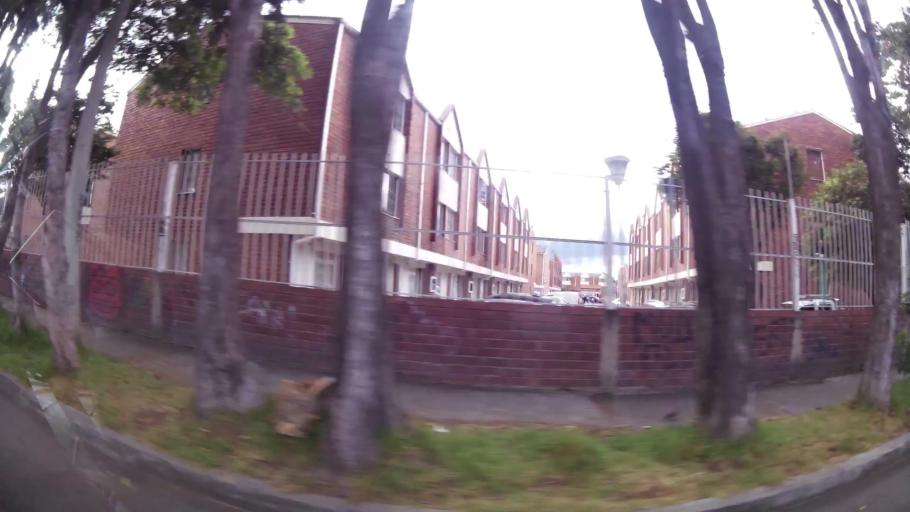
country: CO
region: Bogota D.C.
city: Bogota
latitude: 4.6068
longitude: -74.1204
